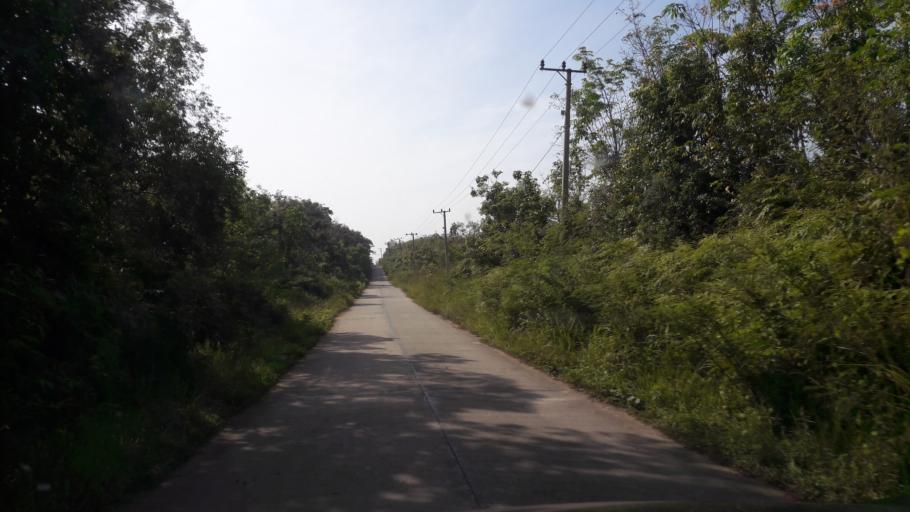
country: ID
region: South Sumatra
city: Gunungmenang
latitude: -3.3119
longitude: 104.0003
